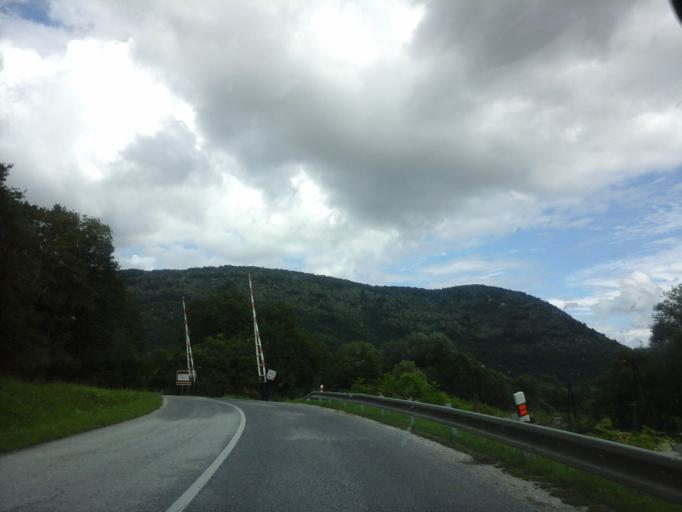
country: SK
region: Kosicky
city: Roznava
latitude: 48.5505
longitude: 20.3992
